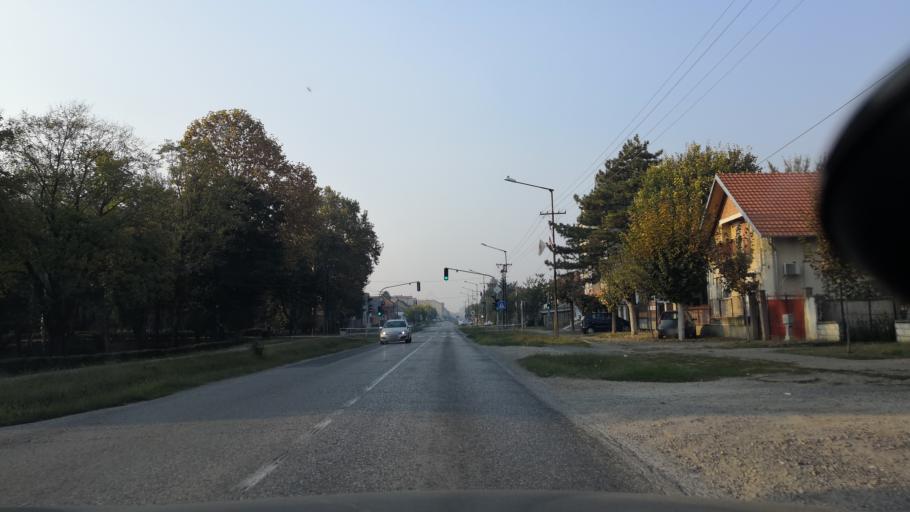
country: RS
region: Autonomna Pokrajina Vojvodina
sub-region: Sremski Okrug
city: Ingija
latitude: 45.0378
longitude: 20.0917
